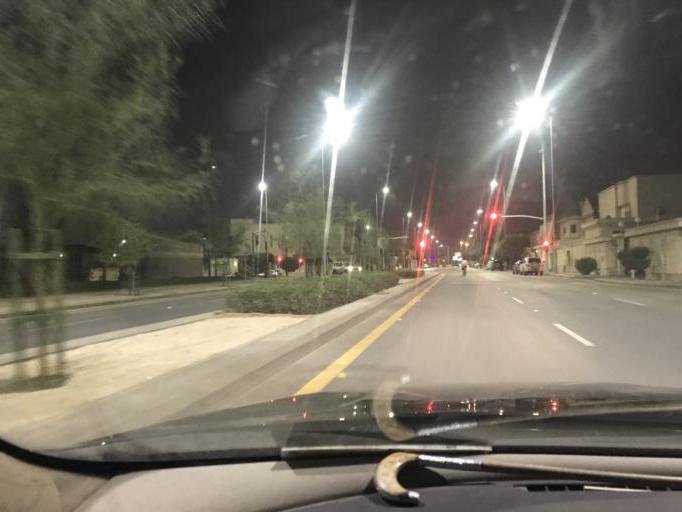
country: SA
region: Ar Riyad
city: Riyadh
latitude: 24.7265
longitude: 46.7895
